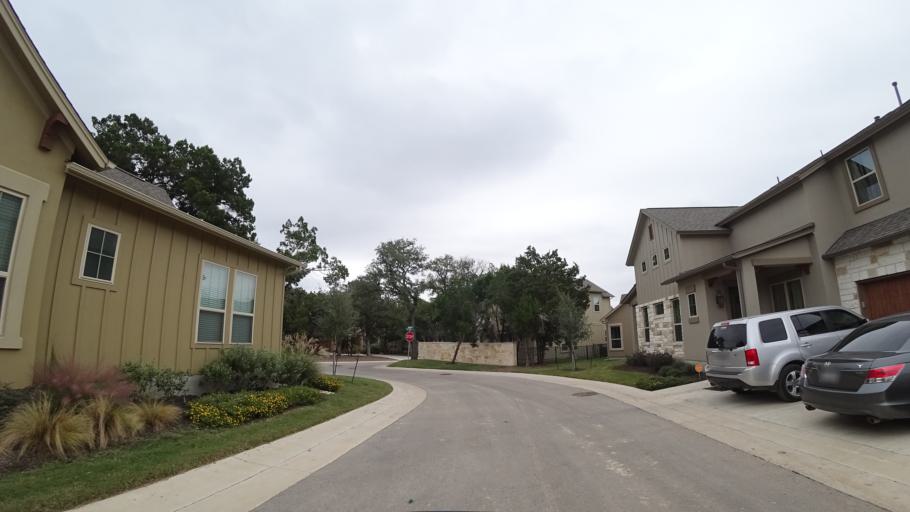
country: US
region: Texas
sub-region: Travis County
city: Manchaca
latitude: 30.1473
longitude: -97.8517
